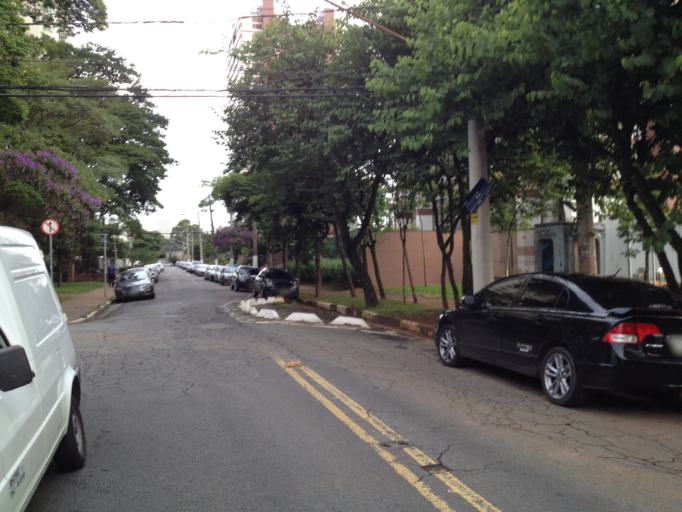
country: BR
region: Sao Paulo
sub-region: Taboao Da Serra
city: Taboao da Serra
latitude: -23.6333
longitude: -46.7150
